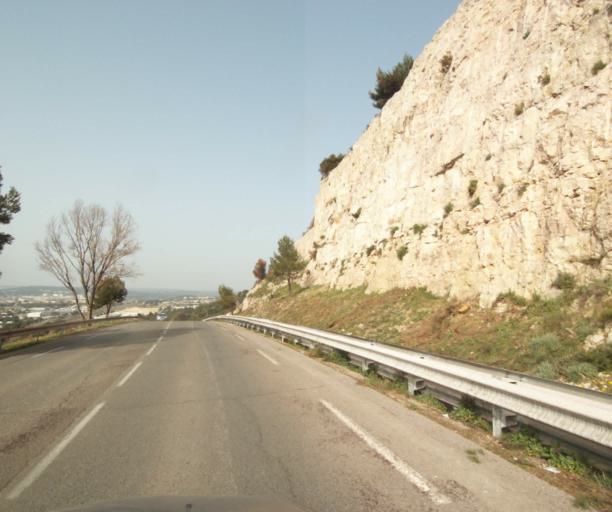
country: FR
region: Provence-Alpes-Cote d'Azur
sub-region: Departement des Bouches-du-Rhone
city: Vitrolles
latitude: 43.4641
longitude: 5.2364
